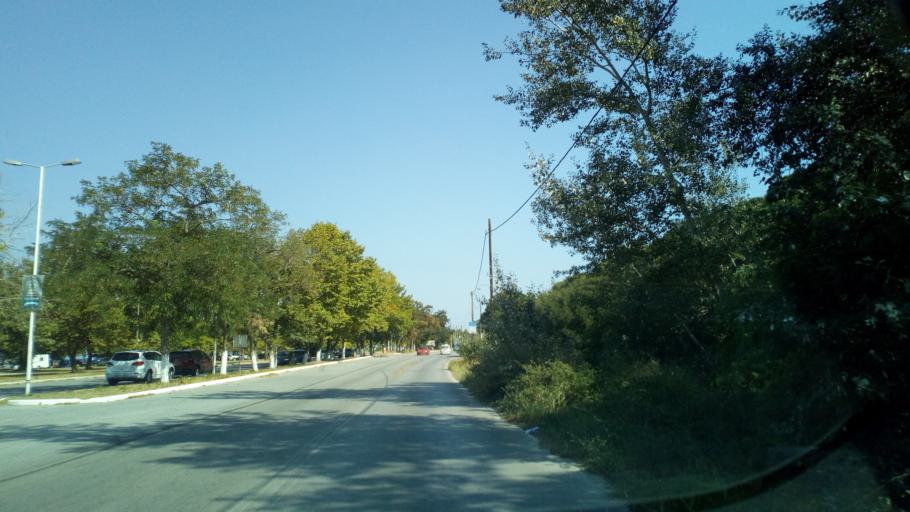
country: GR
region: Central Macedonia
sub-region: Nomos Thessalonikis
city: Stavros
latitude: 40.6630
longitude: 23.7152
